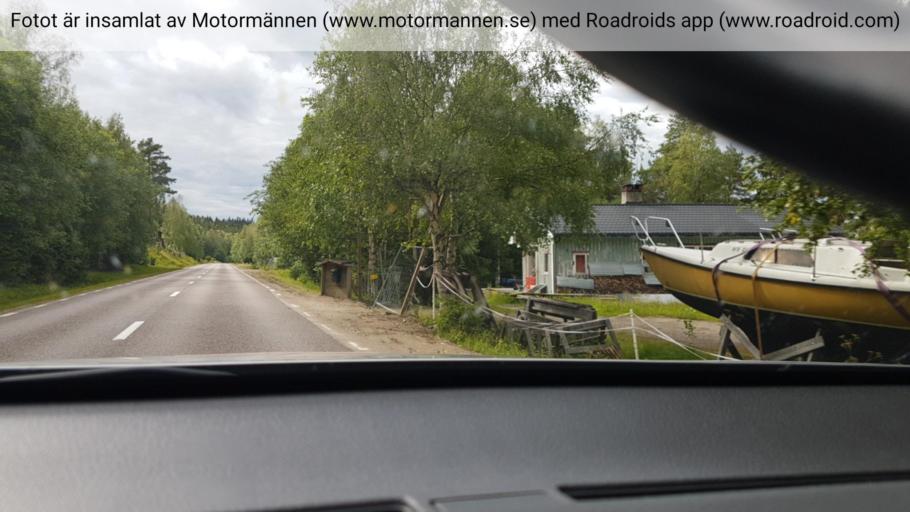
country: NO
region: Hedmark
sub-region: Trysil
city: Innbygda
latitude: 60.8993
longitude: 12.5844
